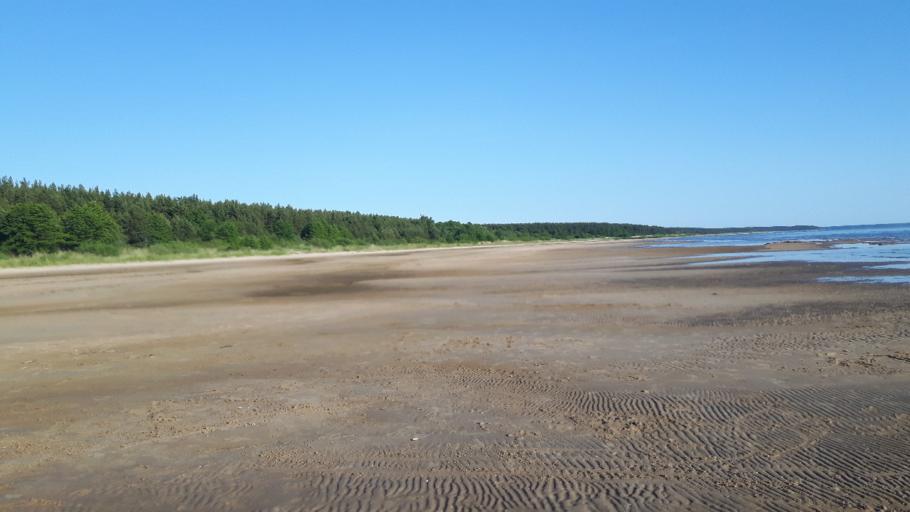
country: LV
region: Salacgrivas
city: Salacgriva
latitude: 57.6920
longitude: 24.3527
